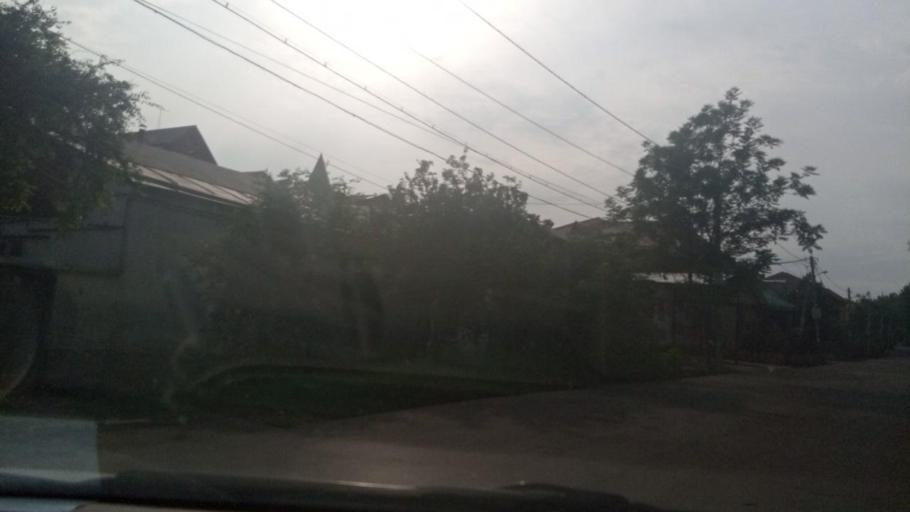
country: UZ
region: Toshkent
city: Salor
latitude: 41.3343
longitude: 69.3576
